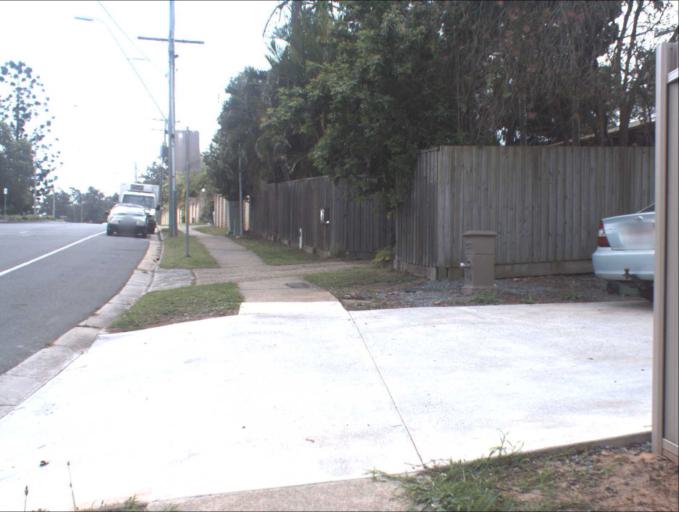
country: AU
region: Queensland
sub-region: Brisbane
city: Sunnybank Hills
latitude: -27.6553
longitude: 153.0404
